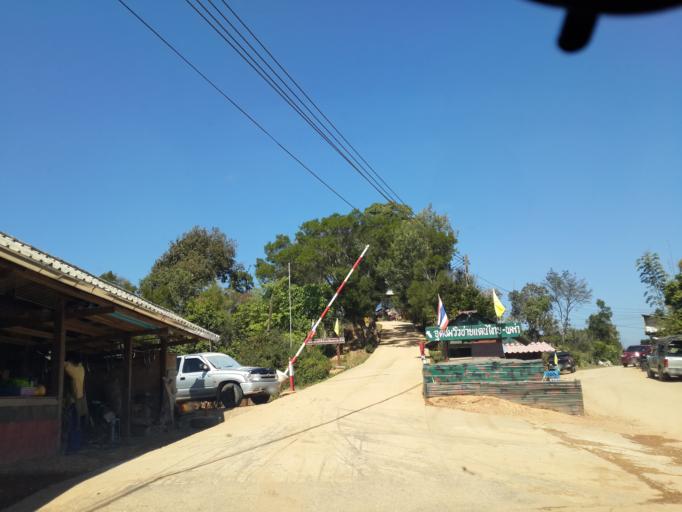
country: TH
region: Chiang Mai
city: Fang
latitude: 19.9385
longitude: 99.0415
